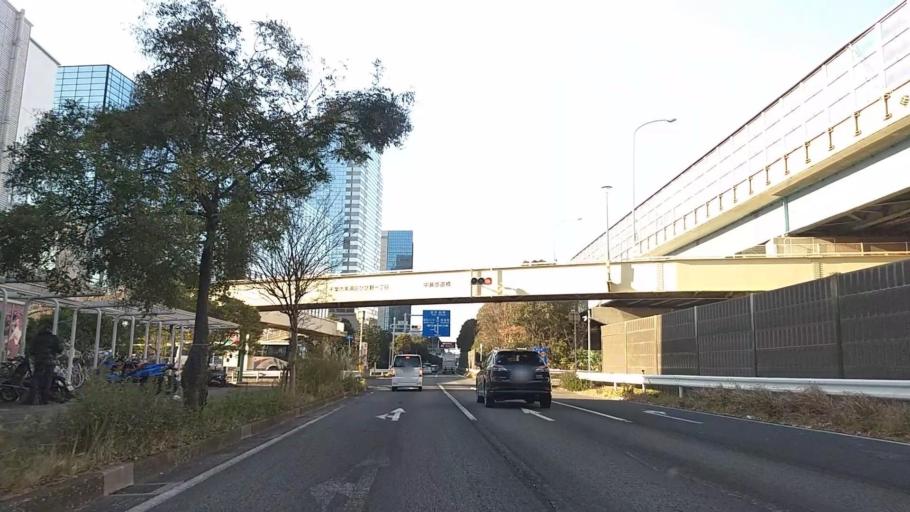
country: JP
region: Chiba
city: Funabashi
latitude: 35.6527
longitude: 140.0455
